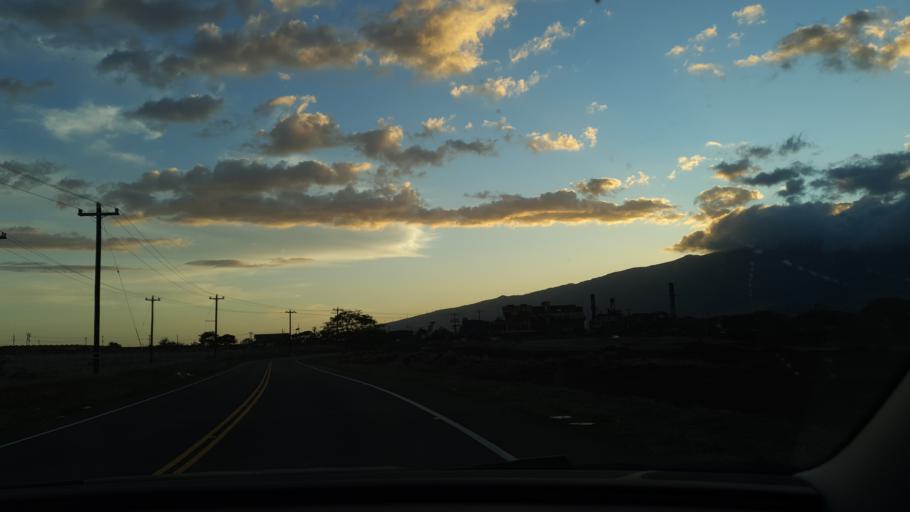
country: US
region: Hawaii
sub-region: Maui County
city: Kahului
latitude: 20.8705
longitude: -156.4477
